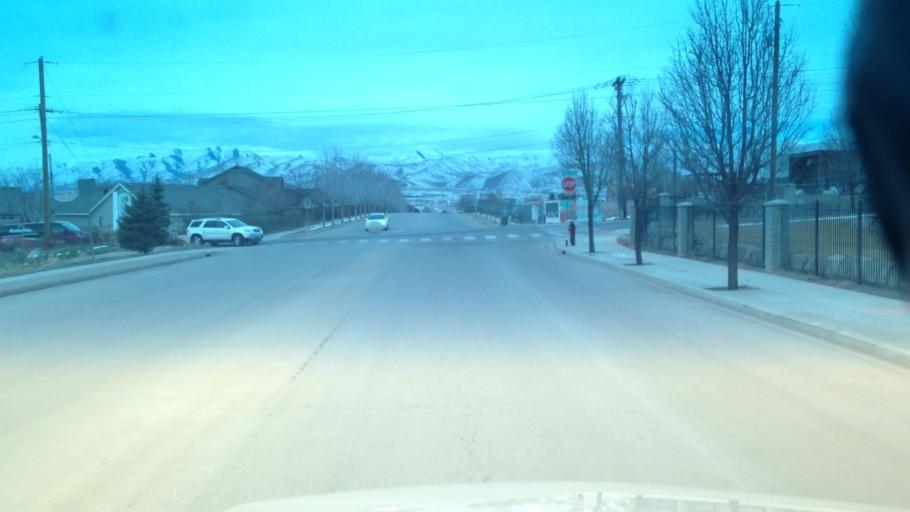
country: US
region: Utah
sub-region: Utah County
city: Lehi
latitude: 40.4280
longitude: -111.8682
